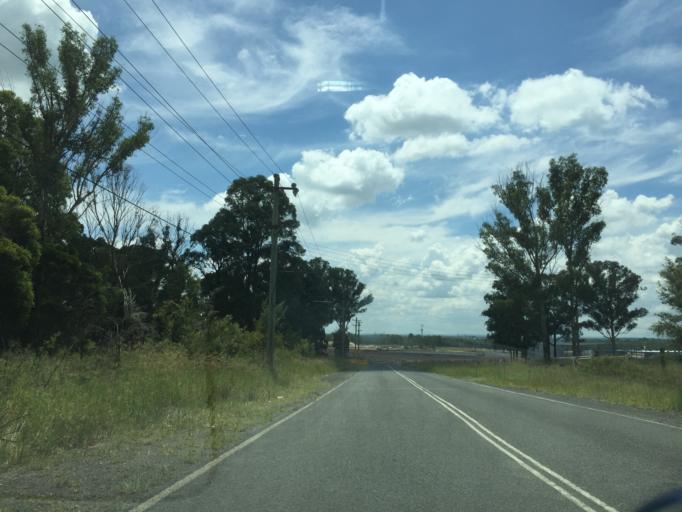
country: AU
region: New South Wales
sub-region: Blacktown
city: Hassall Grove
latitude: -33.7211
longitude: 150.8345
